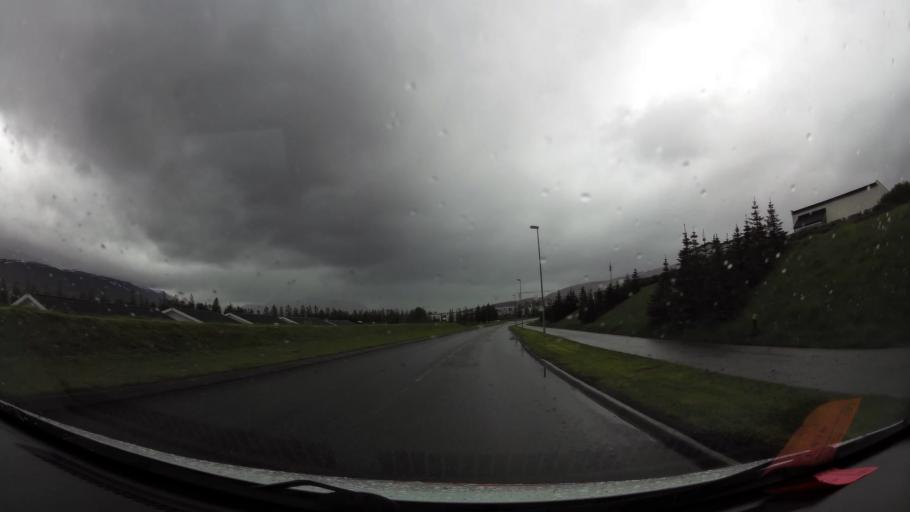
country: IS
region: Northeast
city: Akureyri
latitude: 65.6702
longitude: -18.0957
